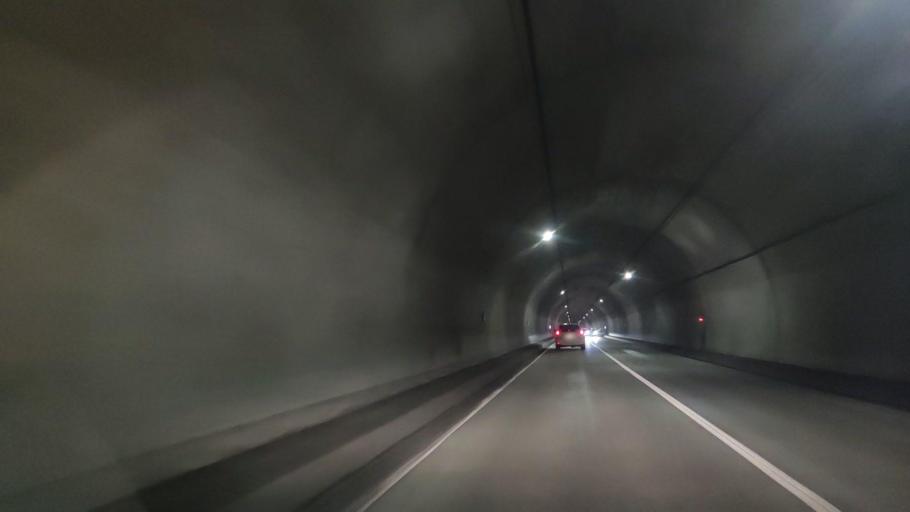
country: JP
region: Hokkaido
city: Ishikari
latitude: 43.5326
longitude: 141.3934
